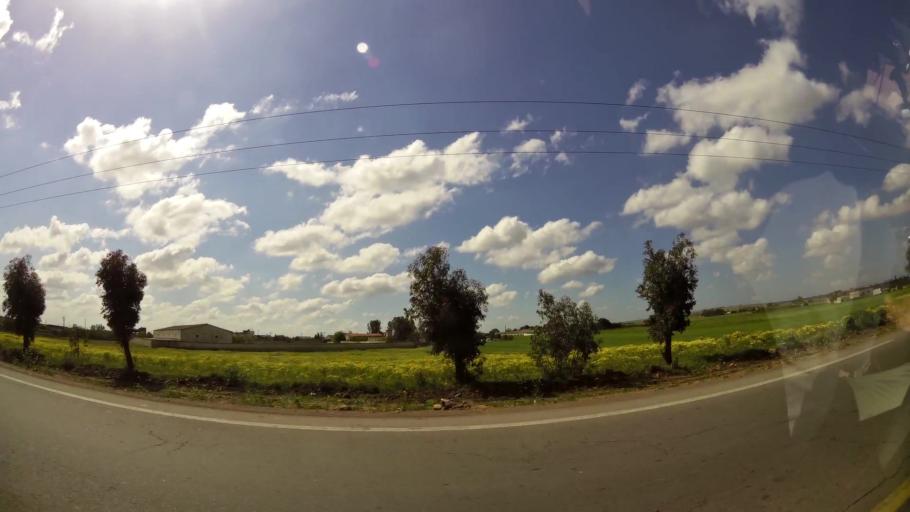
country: MA
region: Grand Casablanca
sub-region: Mediouna
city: Mediouna
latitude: 33.4142
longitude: -7.5318
